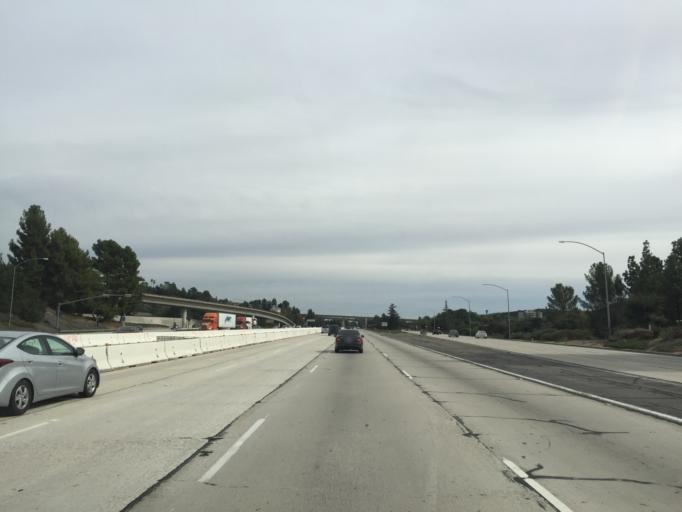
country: US
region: California
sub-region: Los Angeles County
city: La Crescenta-Montrose
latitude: 34.2112
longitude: -118.2269
